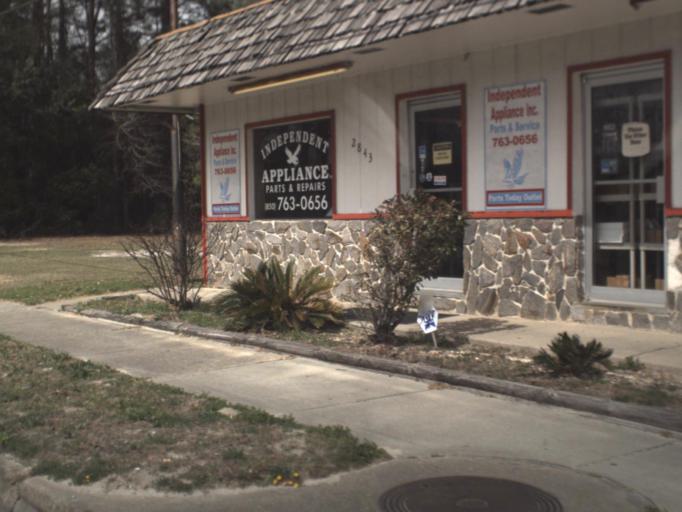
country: US
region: Florida
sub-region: Bay County
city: Cedar Grove
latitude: 30.1750
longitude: -85.6207
